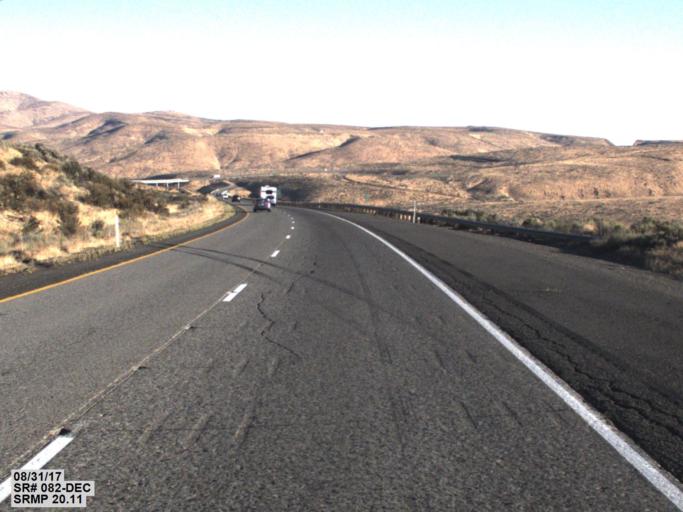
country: US
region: Washington
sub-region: Yakima County
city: Terrace Heights
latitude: 46.7344
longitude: -120.3847
